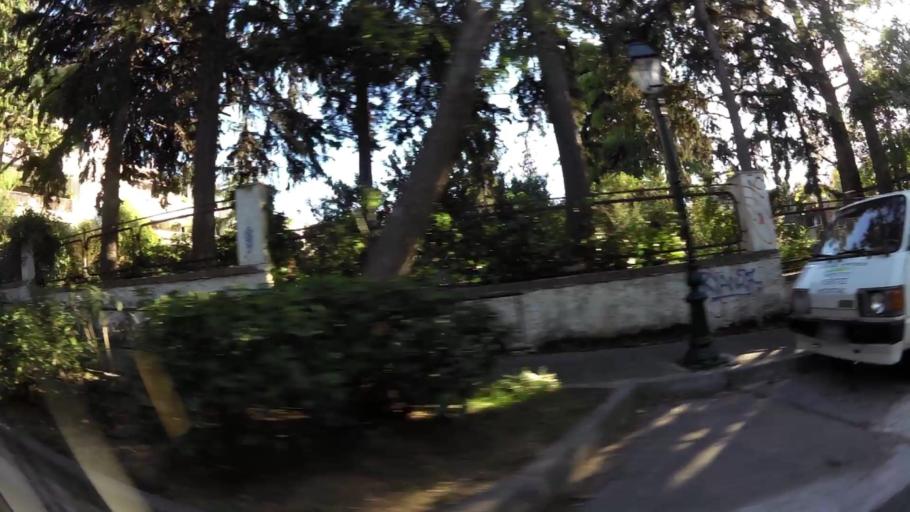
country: GR
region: Attica
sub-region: Nomarchia Athinas
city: Kifisia
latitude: 38.0750
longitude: 23.8090
